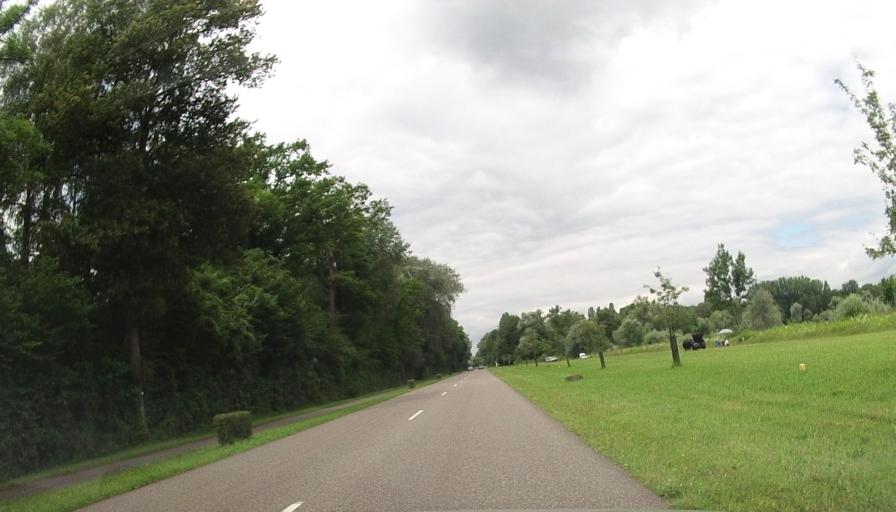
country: FR
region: Alsace
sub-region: Departement du Bas-Rhin
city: Seltz
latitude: 48.8897
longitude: 8.1240
